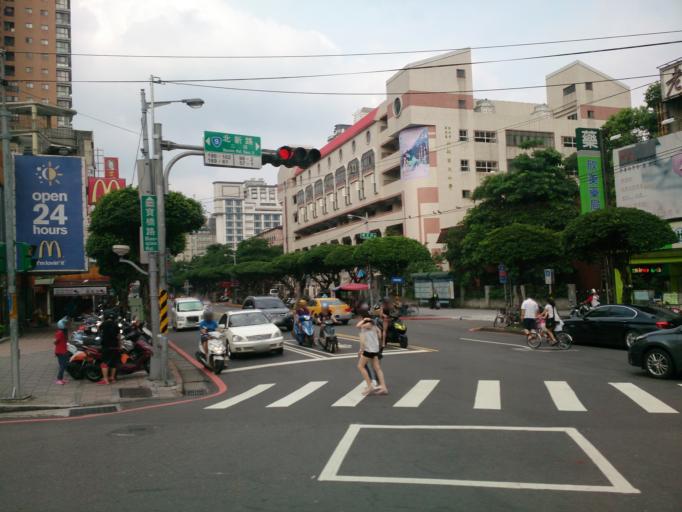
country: TW
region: Taipei
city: Taipei
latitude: 24.9734
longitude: 121.5430
